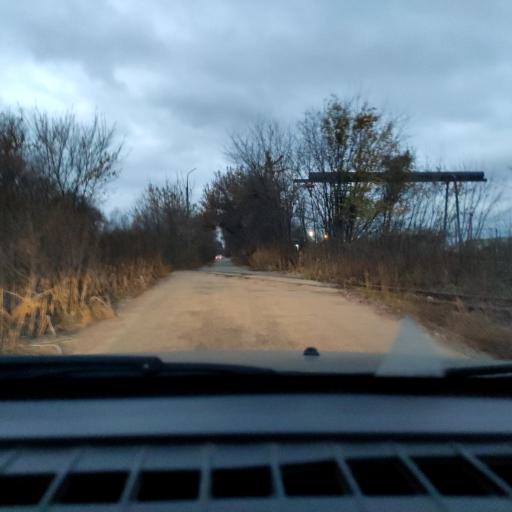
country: RU
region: Samara
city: Tol'yatti
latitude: 53.5636
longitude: 49.3179
